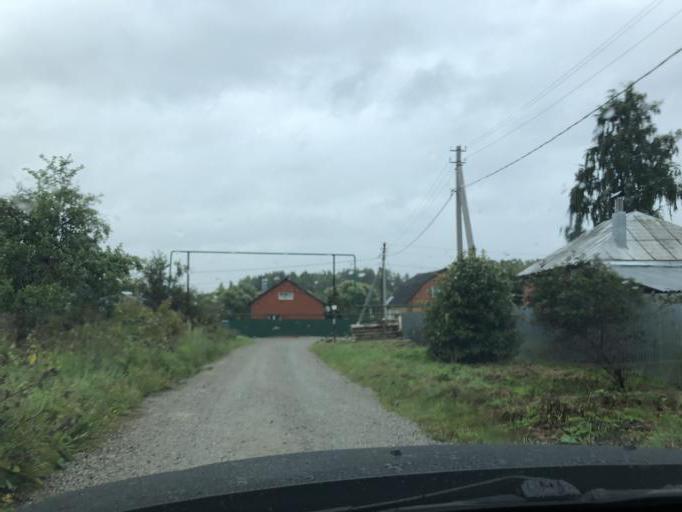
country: RU
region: Tula
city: Gorelki
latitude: 54.2599
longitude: 37.6195
